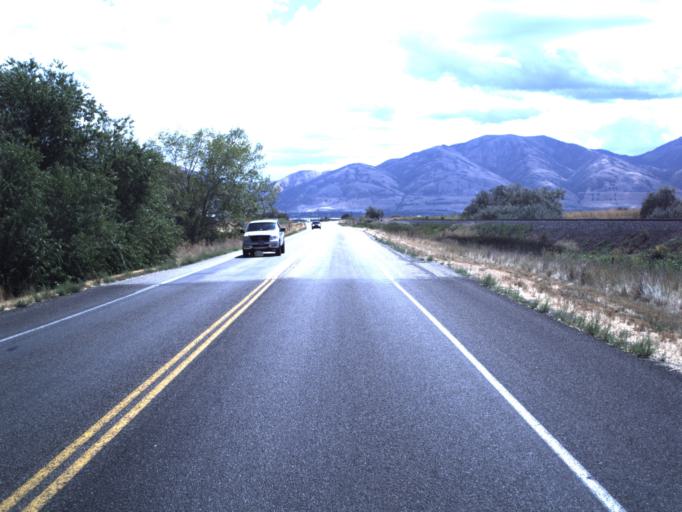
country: US
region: Utah
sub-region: Box Elder County
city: Brigham City
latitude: 41.5440
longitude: -112.0921
